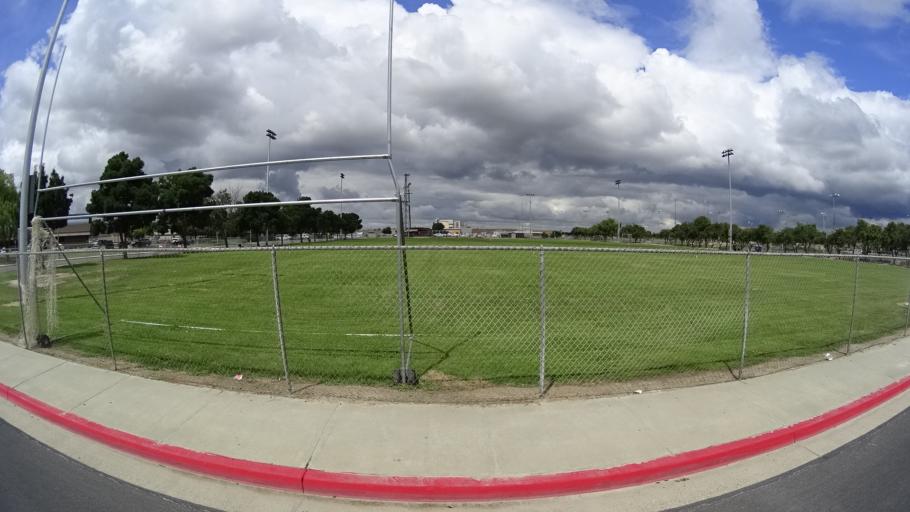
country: US
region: California
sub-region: Kings County
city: Hanford
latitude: 36.3330
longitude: -119.6633
